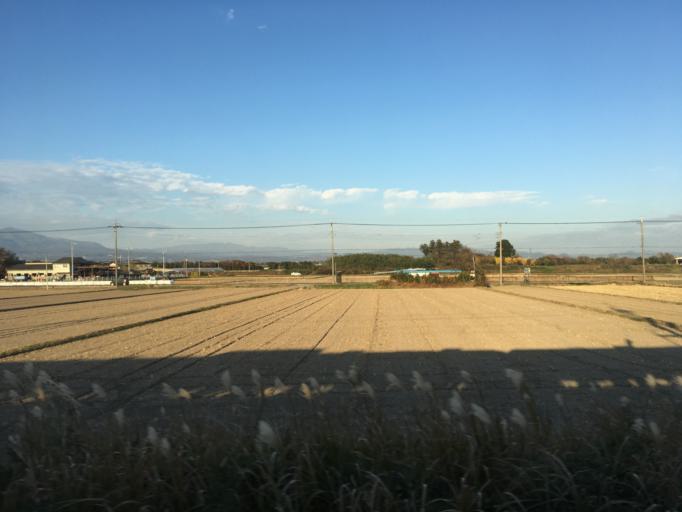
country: JP
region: Gunma
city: Isesaki
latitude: 36.3451
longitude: 139.1613
